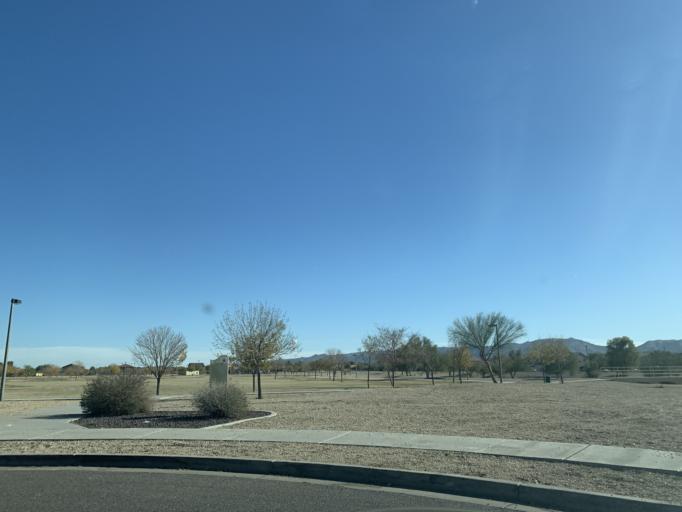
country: US
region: Arizona
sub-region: Maricopa County
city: Laveen
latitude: 33.3975
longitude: -112.1293
